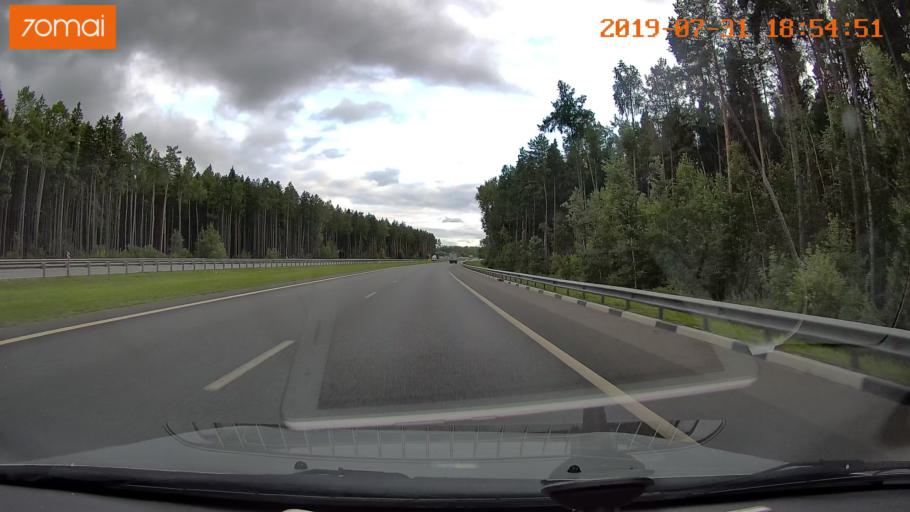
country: RU
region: Moskovskaya
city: Raduzhnyy
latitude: 55.1834
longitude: 38.6695
